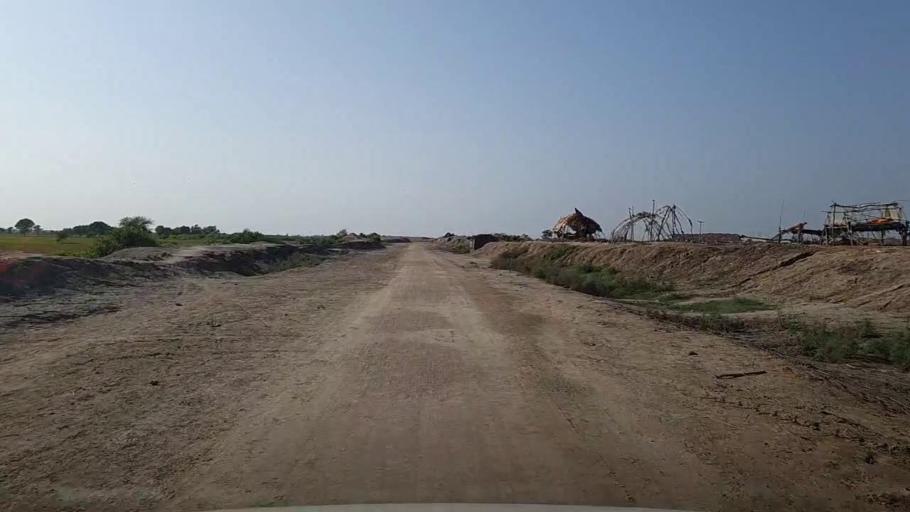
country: PK
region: Sindh
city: Kario
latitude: 24.8210
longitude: 68.4893
